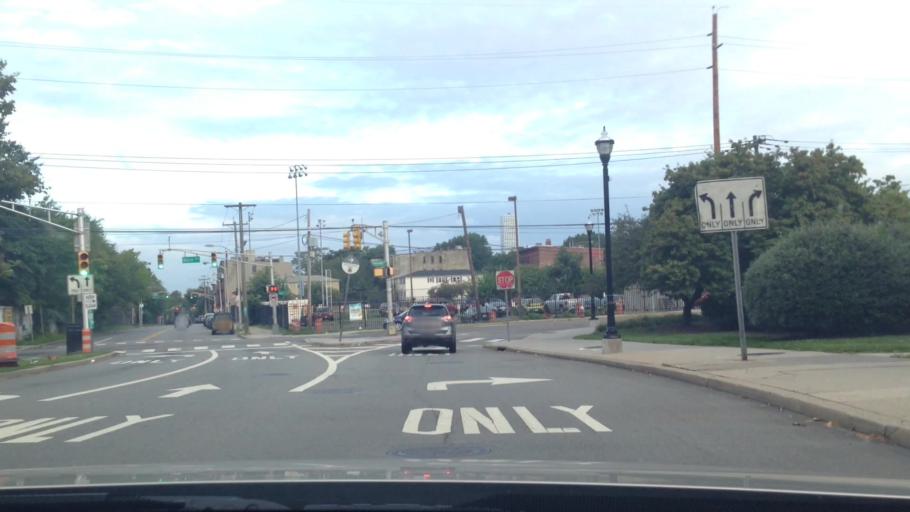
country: US
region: New Jersey
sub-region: Hudson County
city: Hoboken
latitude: 40.7250
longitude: -74.0397
